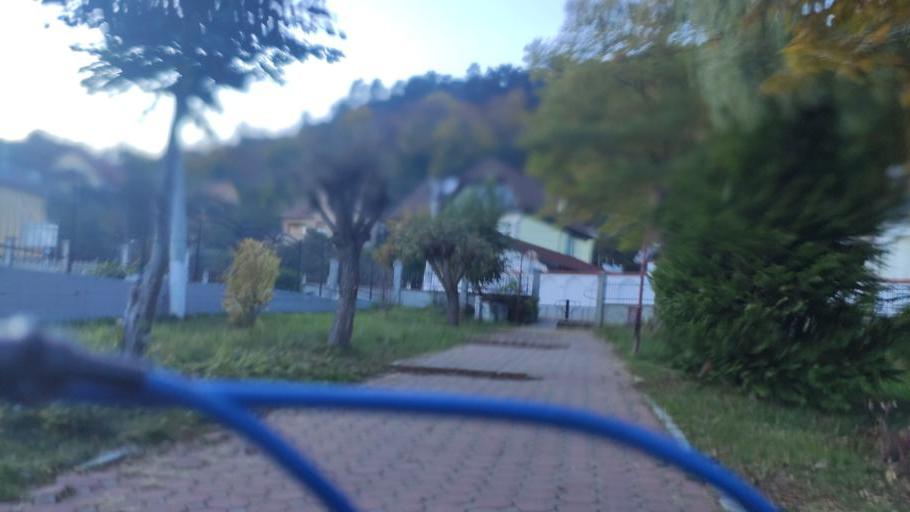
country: RO
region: Brasov
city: Codlea
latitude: 45.7013
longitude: 25.4388
